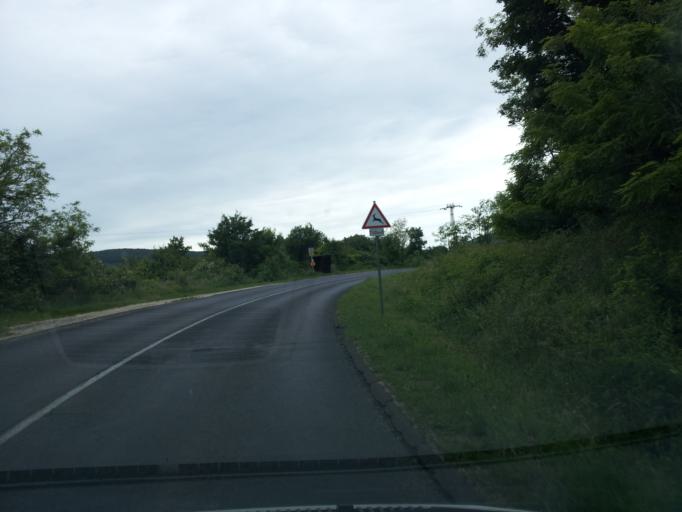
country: HU
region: Pest
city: Csobanka
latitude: 47.6664
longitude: 18.9592
